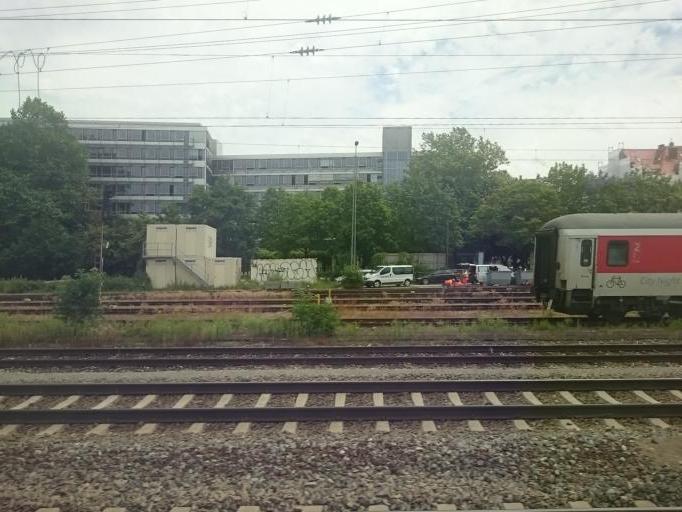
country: DE
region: Bavaria
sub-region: Upper Bavaria
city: Bogenhausen
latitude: 48.1310
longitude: 11.6106
